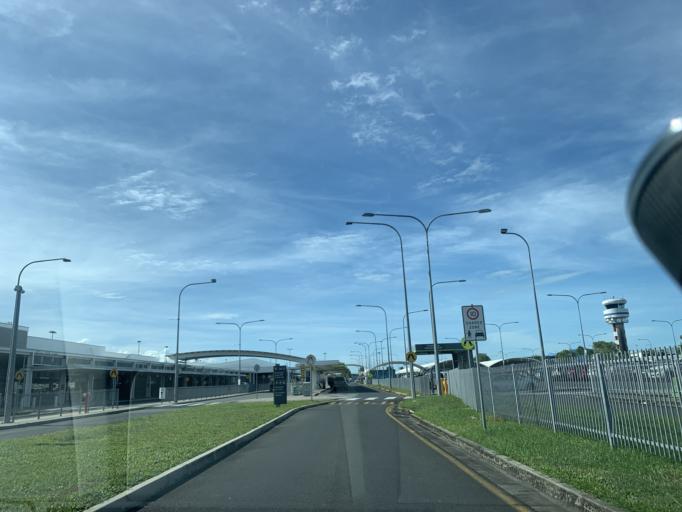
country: AU
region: Queensland
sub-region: Cairns
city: Cairns
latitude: -16.8783
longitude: 145.7550
